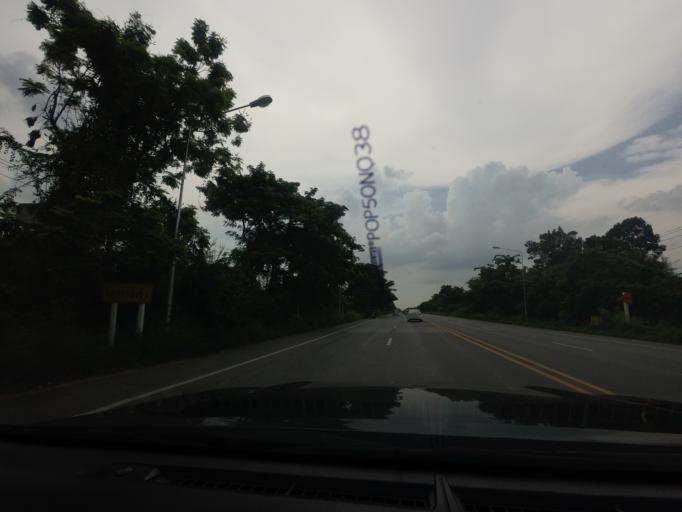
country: TH
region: Nakhon Pathom
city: Kamphaeng Saen
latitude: 14.0095
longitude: 99.9604
